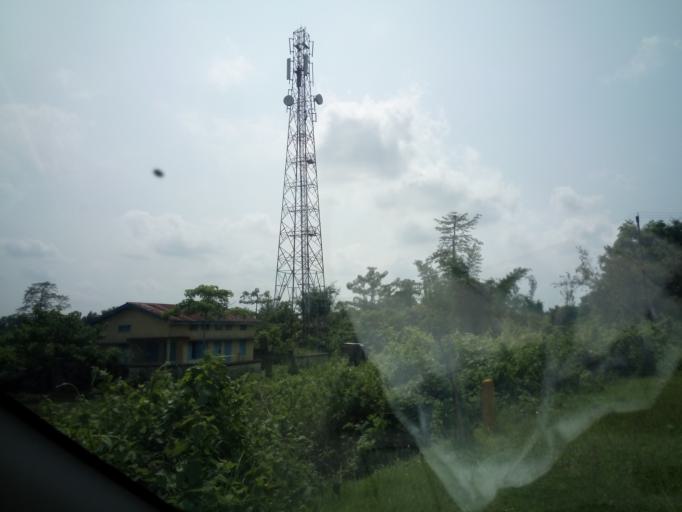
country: IN
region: Assam
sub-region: Udalguri
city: Udalguri
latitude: 26.7400
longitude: 92.1613
